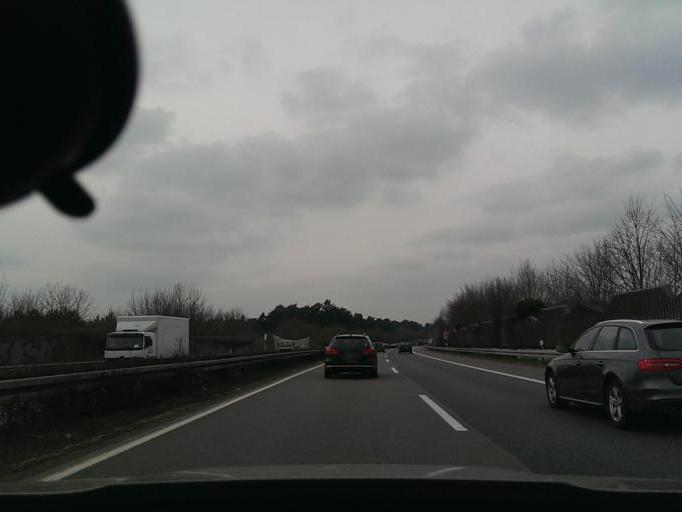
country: DE
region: North Rhine-Westphalia
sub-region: Regierungsbezirk Detmold
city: Verl
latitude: 51.9264
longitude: 8.5842
